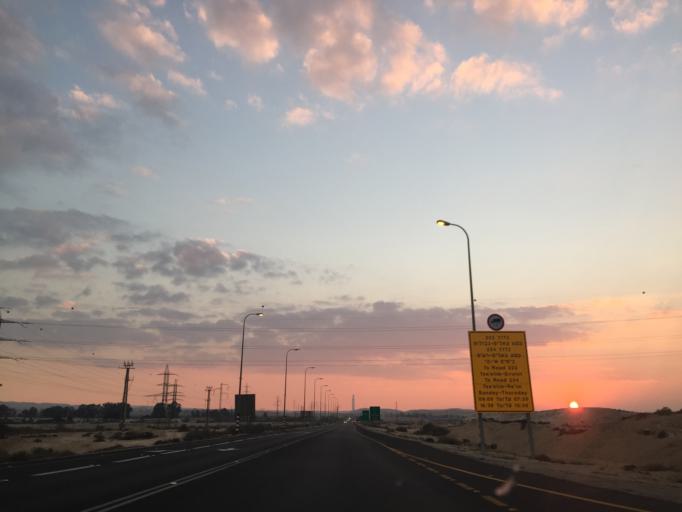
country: IL
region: Southern District
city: Yeroham
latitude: 31.0148
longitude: 34.7852
